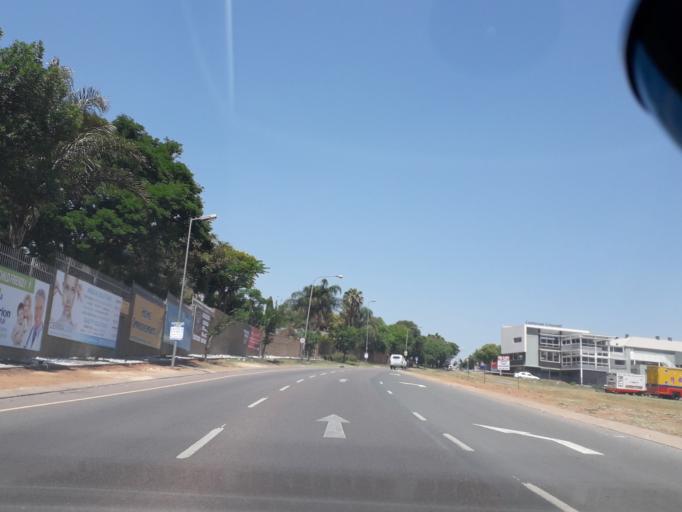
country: ZA
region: Gauteng
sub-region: City of Tshwane Metropolitan Municipality
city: Centurion
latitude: -25.8636
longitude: 28.1865
